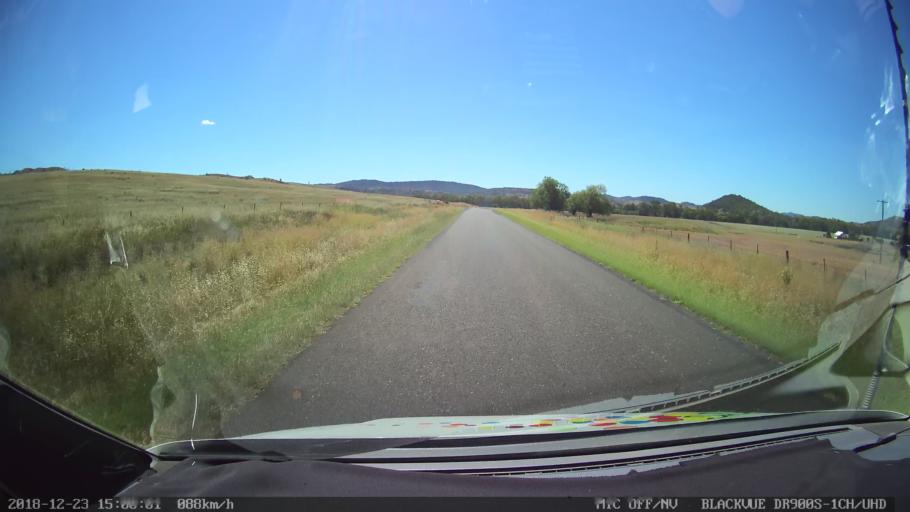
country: AU
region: New South Wales
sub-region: Tamworth Municipality
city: Manilla
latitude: -30.7238
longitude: 150.7928
